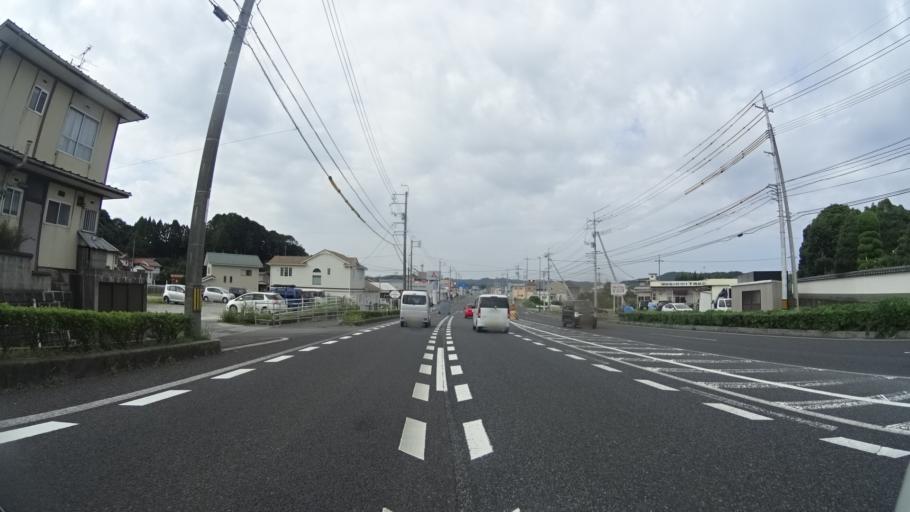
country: JP
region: Shimane
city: Odacho-oda
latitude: 35.2039
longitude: 132.4991
